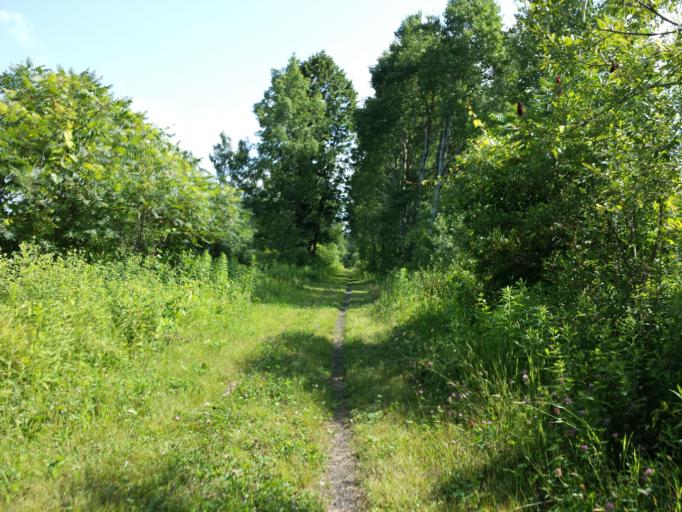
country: US
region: Vermont
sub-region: Rutland County
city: Poultney
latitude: 43.5005
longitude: -73.2412
